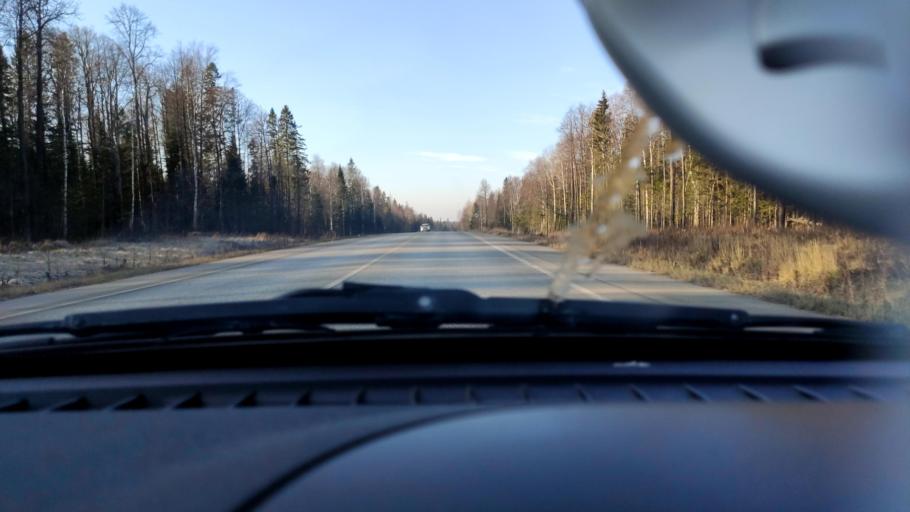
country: RU
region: Perm
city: Novyye Lyady
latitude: 58.0275
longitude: 56.5064
